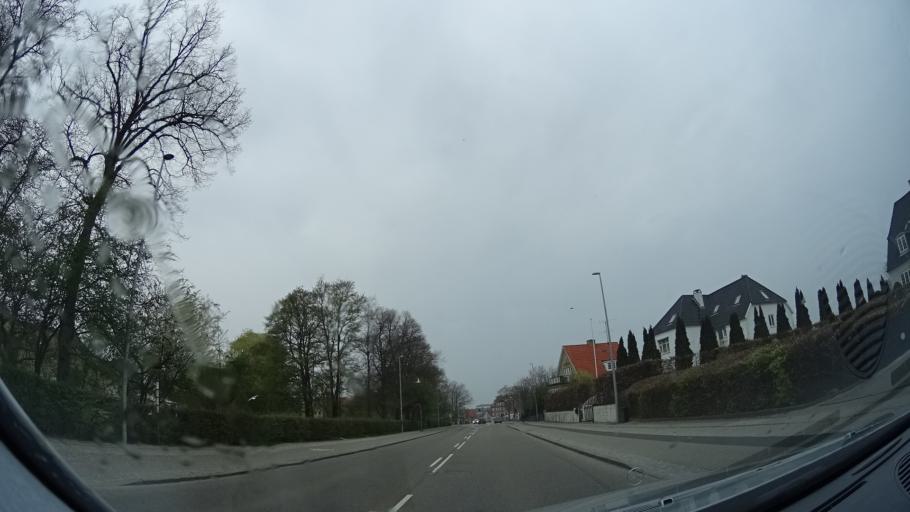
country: DK
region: Zealand
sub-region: Holbaek Kommune
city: Holbaek
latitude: 55.7157
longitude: 11.7269
